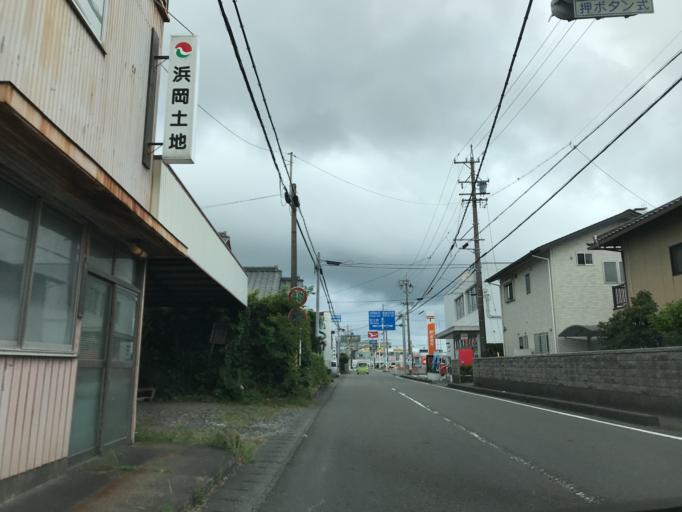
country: JP
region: Shizuoka
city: Sagara
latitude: 34.6501
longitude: 138.1286
